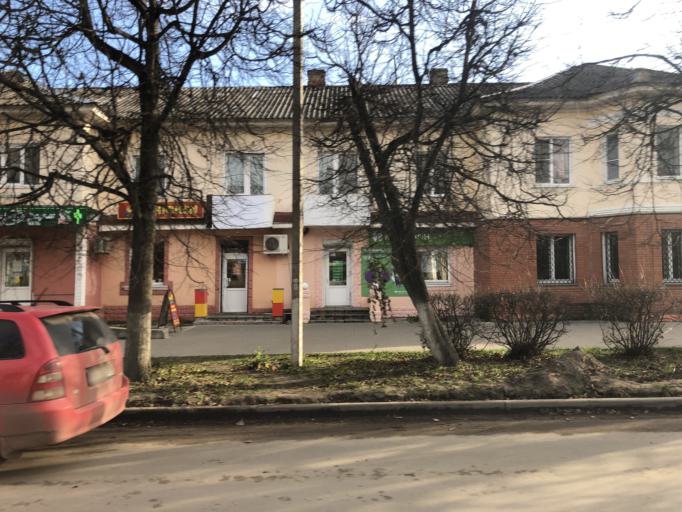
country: RU
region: Tverskaya
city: Rzhev
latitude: 56.2508
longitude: 34.3275
